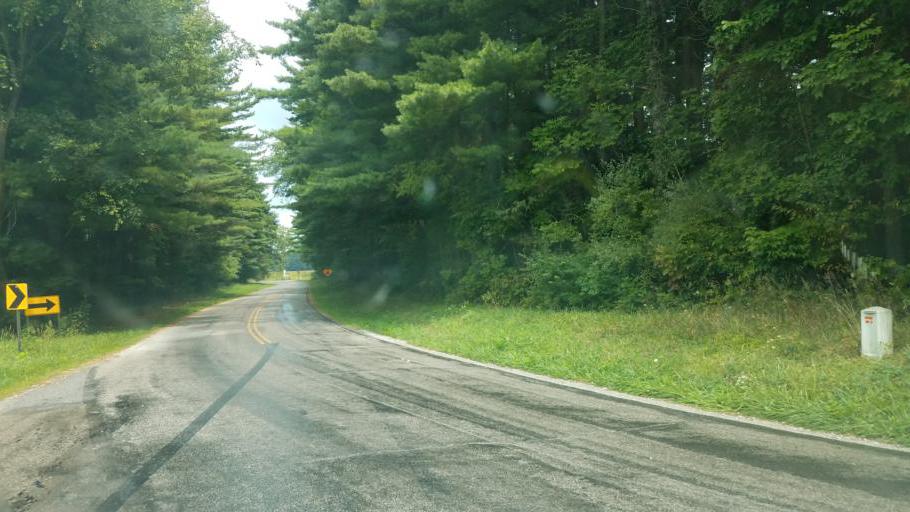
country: US
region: Ohio
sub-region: Ashland County
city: Loudonville
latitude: 40.6296
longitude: -82.3481
